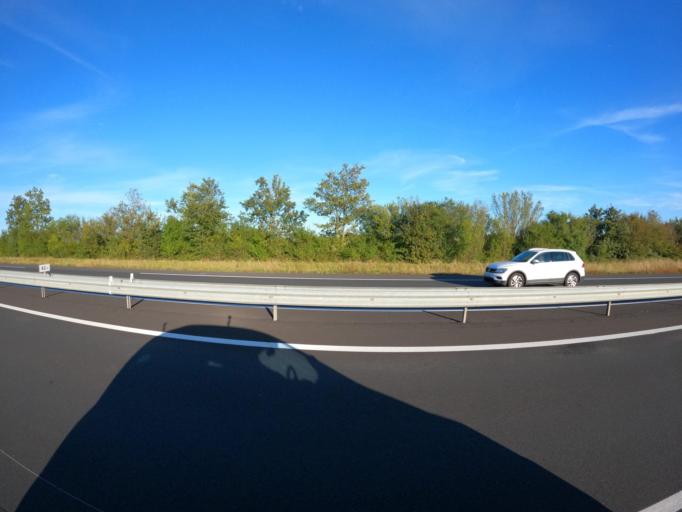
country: FR
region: Pays de la Loire
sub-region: Departement de la Vendee
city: Saint-Laurent-sur-Sevre
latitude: 46.9745
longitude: -0.9177
